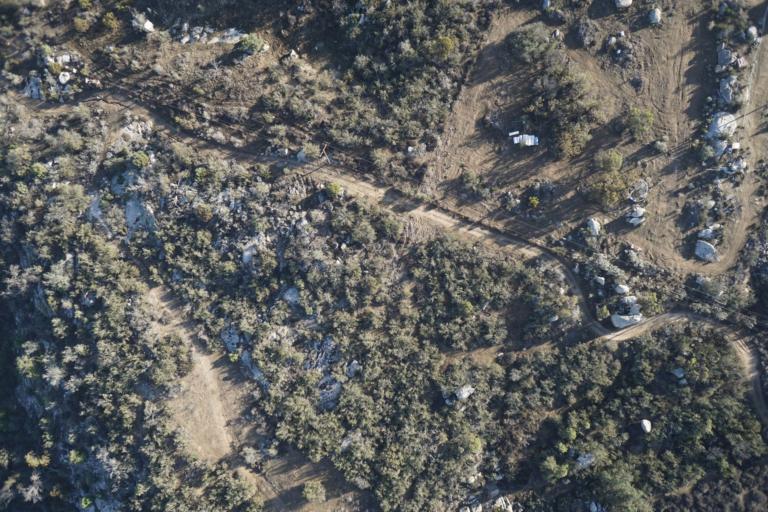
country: US
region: California
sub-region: Riverside County
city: East Hemet
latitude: 33.6183
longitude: -116.9050
